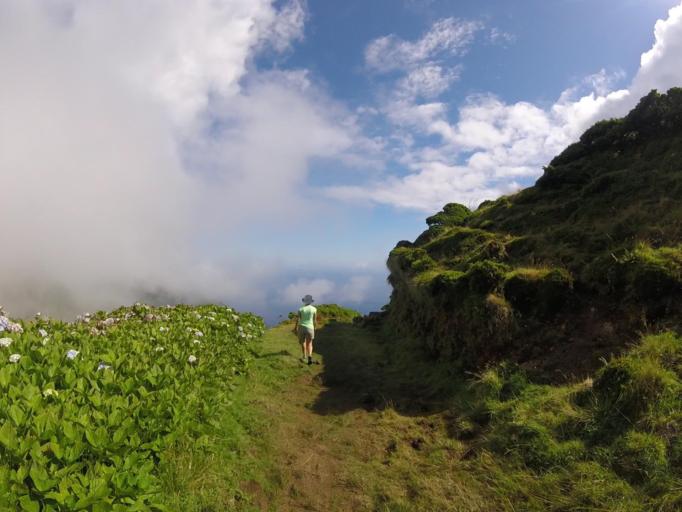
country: PT
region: Azores
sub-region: Sao Roque do Pico
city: Sao Roque do Pico
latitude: 38.5990
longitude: -27.9241
